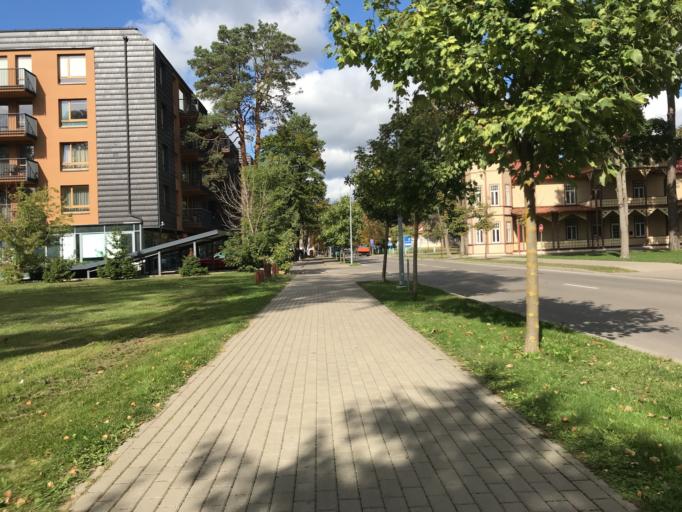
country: LT
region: Alytaus apskritis
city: Druskininkai
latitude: 54.0226
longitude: 23.9704
